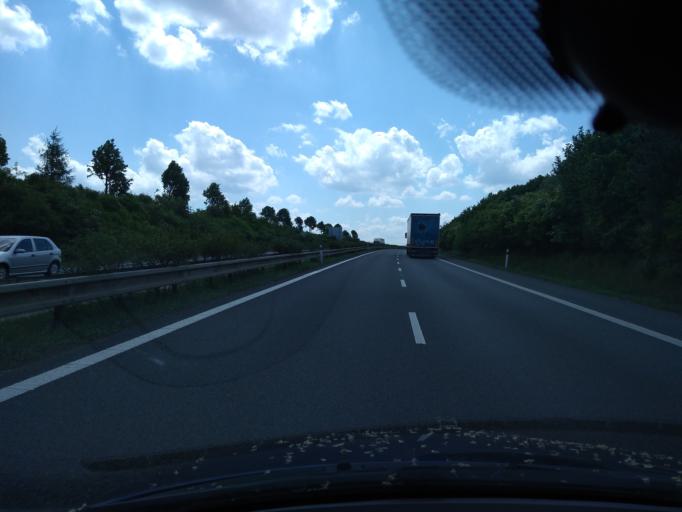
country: CZ
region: Plzensky
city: Stenovice
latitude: 49.6930
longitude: 13.3667
